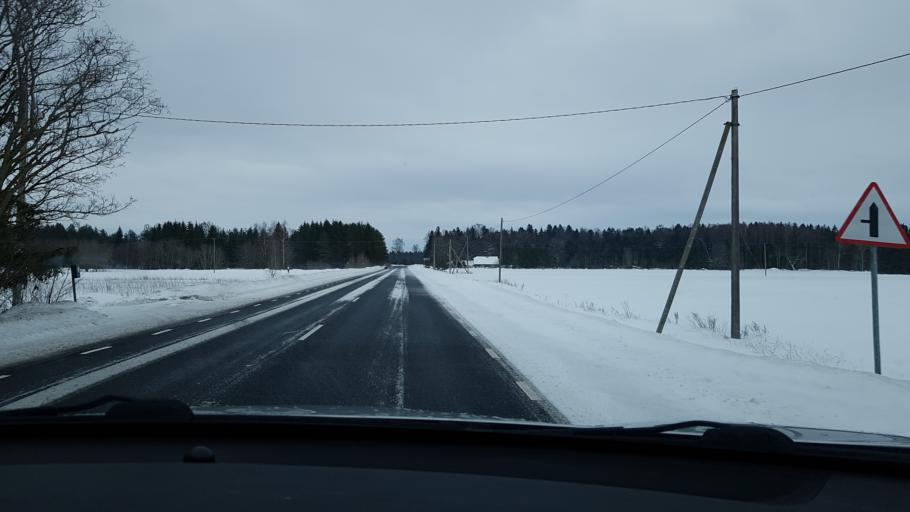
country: EE
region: Jaervamaa
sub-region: Jaerva-Jaani vald
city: Jarva-Jaani
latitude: 59.1073
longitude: 25.8045
